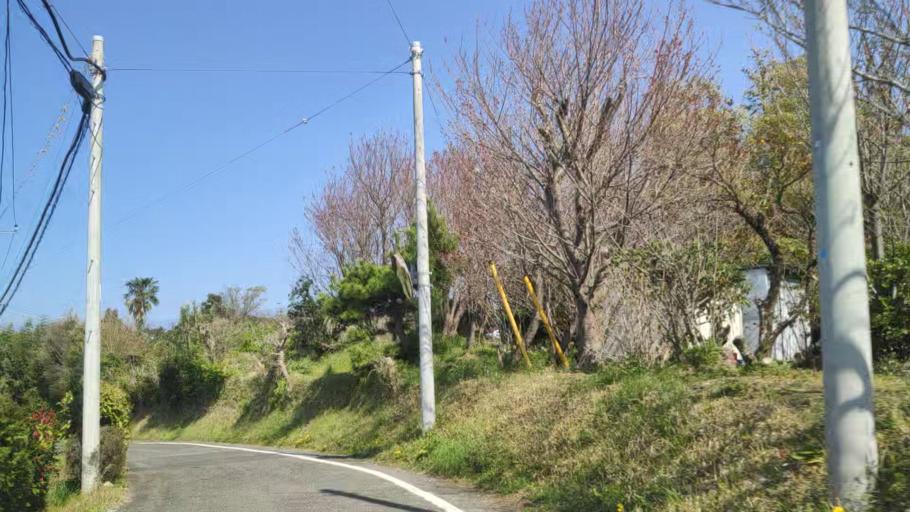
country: JP
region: Kanagawa
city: Ninomiya
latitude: 35.3256
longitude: 139.2577
